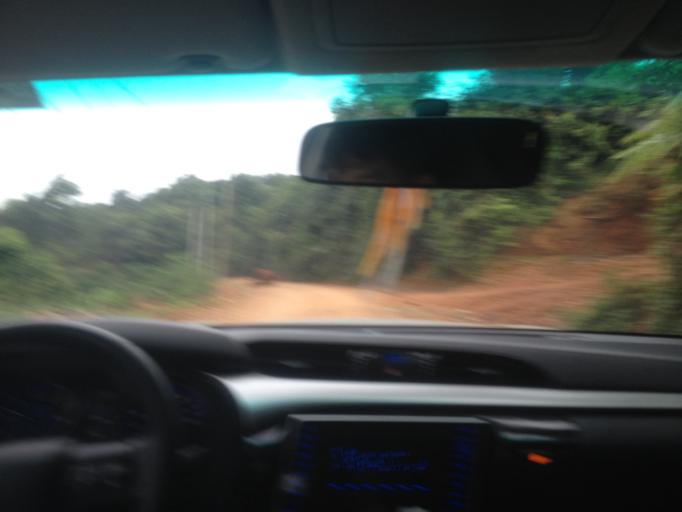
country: TH
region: Nan
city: Chaloem Phra Kiat
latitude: 19.9786
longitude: 101.1420
